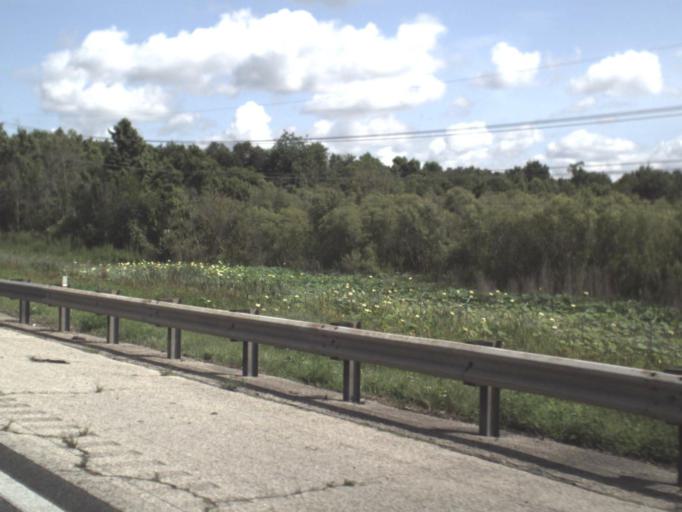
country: US
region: Florida
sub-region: Alachua County
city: Gainesville
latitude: 29.6455
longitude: -82.4068
